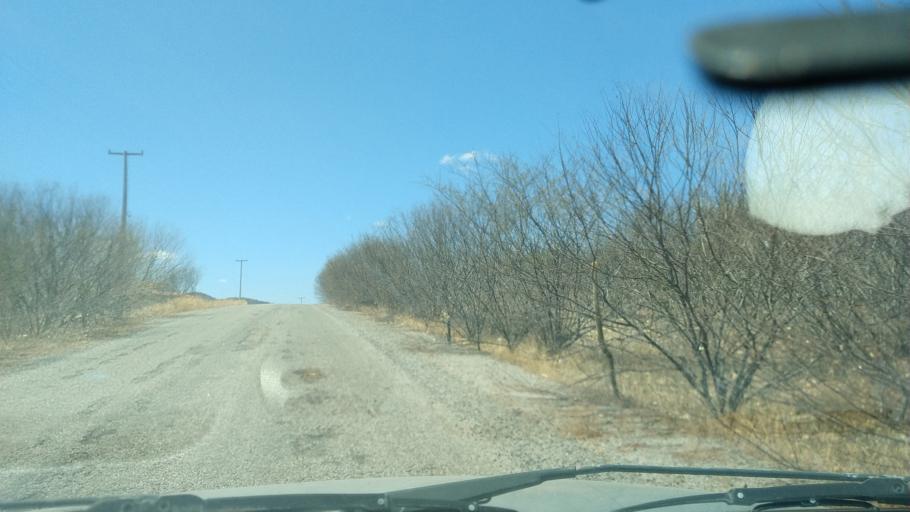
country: BR
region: Rio Grande do Norte
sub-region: Sao Tome
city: Sao Tome
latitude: -5.9763
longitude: -36.1438
